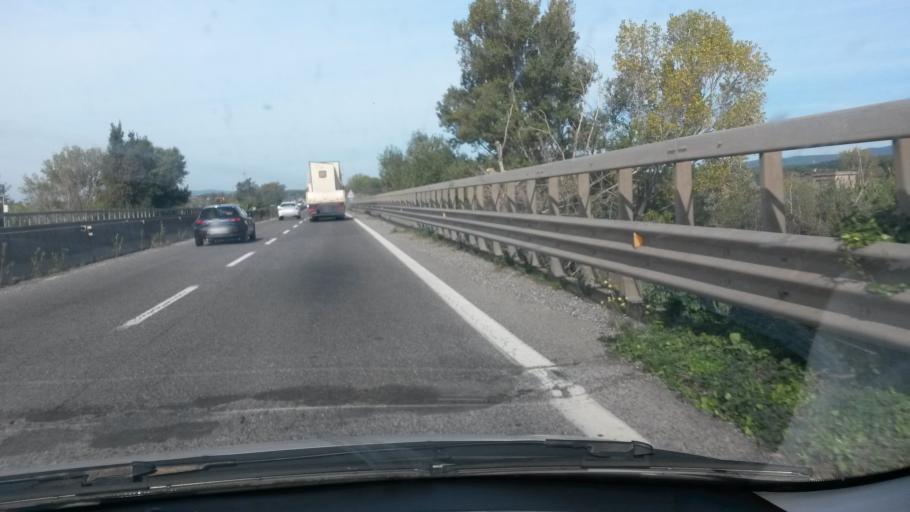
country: IT
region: Tuscany
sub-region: Provincia di Livorno
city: Cecina
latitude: 43.3230
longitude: 10.5312
